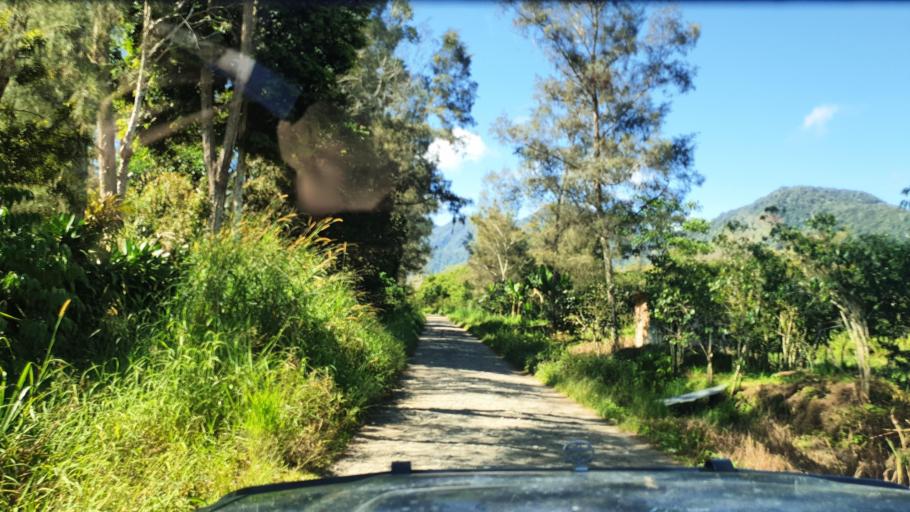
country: PG
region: Western Highlands
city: Rauna
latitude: -5.8149
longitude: 144.3795
